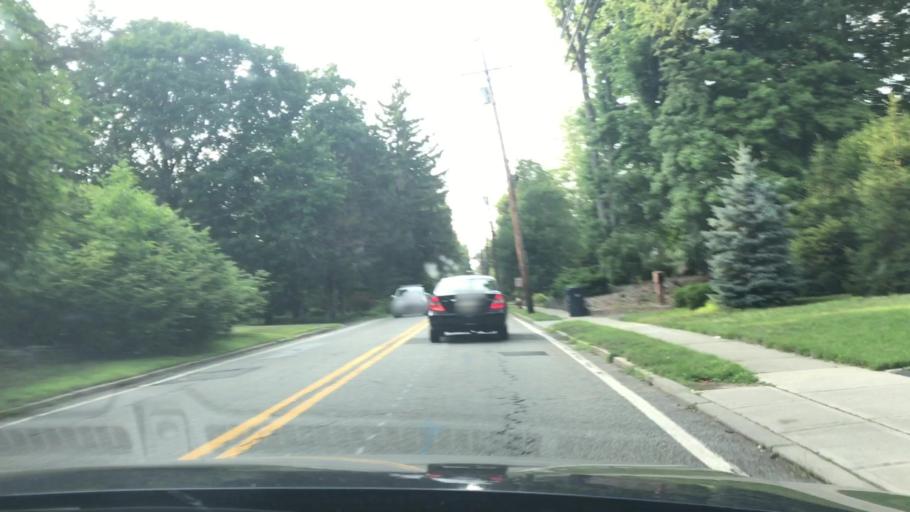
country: US
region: New Jersey
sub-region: Bergen County
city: Norwood
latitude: 40.9879
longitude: -73.9619
